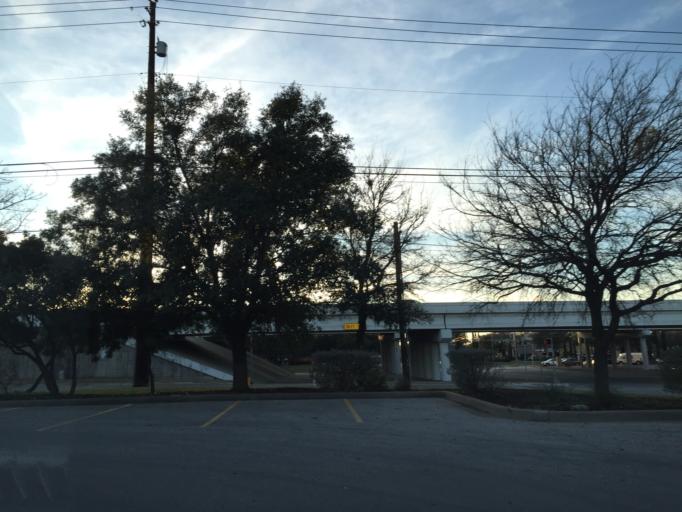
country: US
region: Texas
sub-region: Williamson County
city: Jollyville
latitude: 30.3938
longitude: -97.7457
